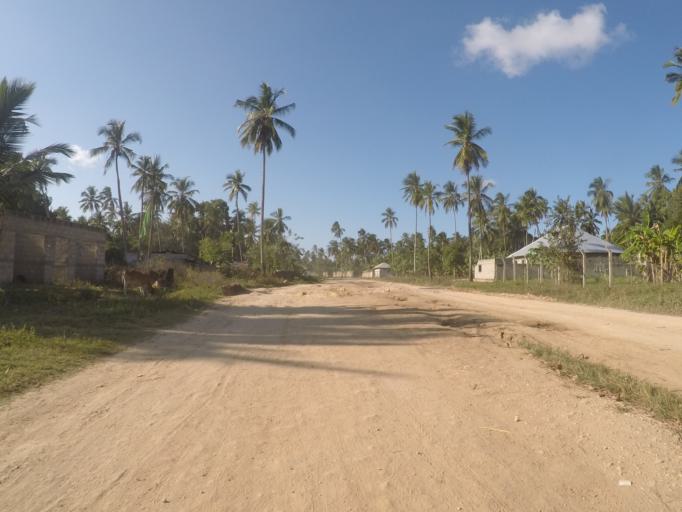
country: TZ
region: Zanzibar Central/South
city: Koani
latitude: -6.1671
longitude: 39.2864
